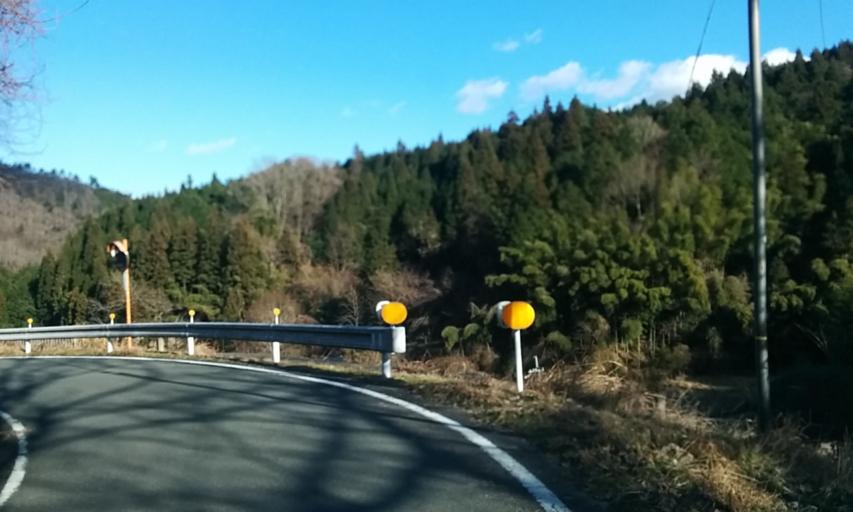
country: JP
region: Kyoto
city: Fukuchiyama
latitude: 35.2741
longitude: 135.0159
